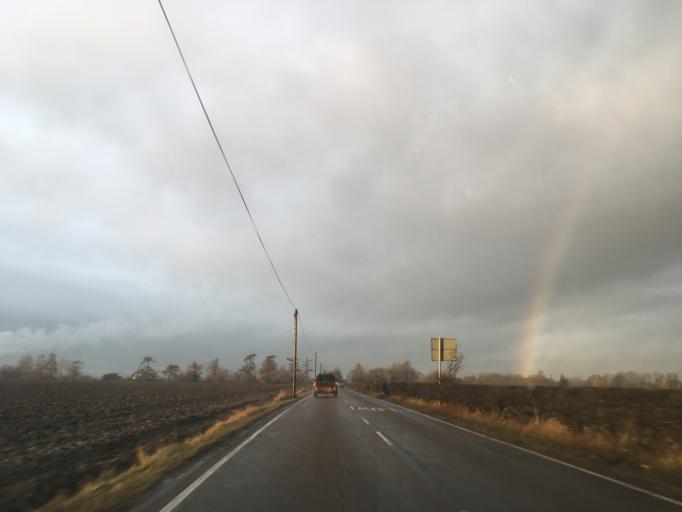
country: GB
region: Scotland
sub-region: Clackmannanshire
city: Alloa
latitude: 56.0971
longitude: -3.8160
